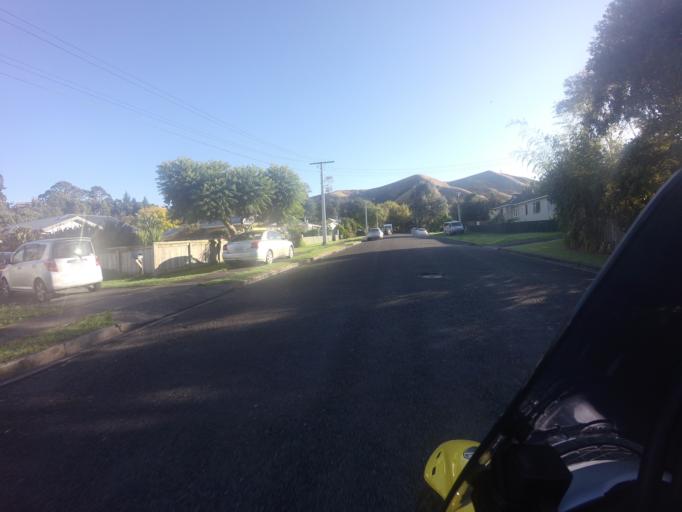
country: NZ
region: Gisborne
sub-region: Gisborne District
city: Gisborne
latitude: -38.6667
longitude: 178.0584
